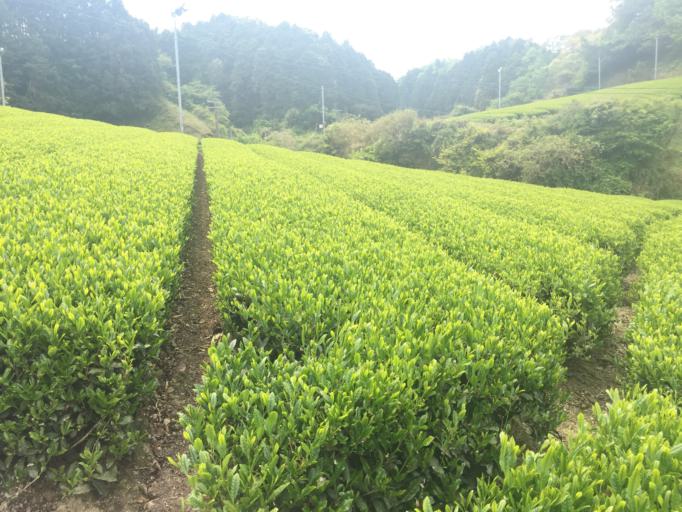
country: JP
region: Shizuoka
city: Kakegawa
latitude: 34.7497
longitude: 138.0141
